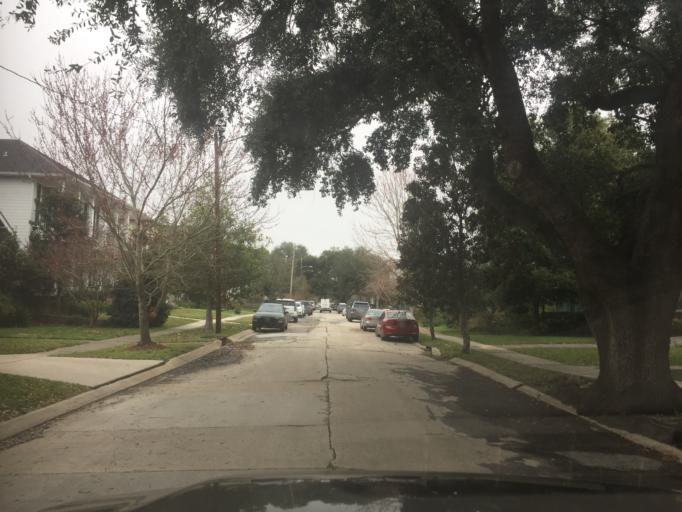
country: US
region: Louisiana
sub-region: Jefferson Parish
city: Metairie
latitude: 30.0145
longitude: -90.1103
